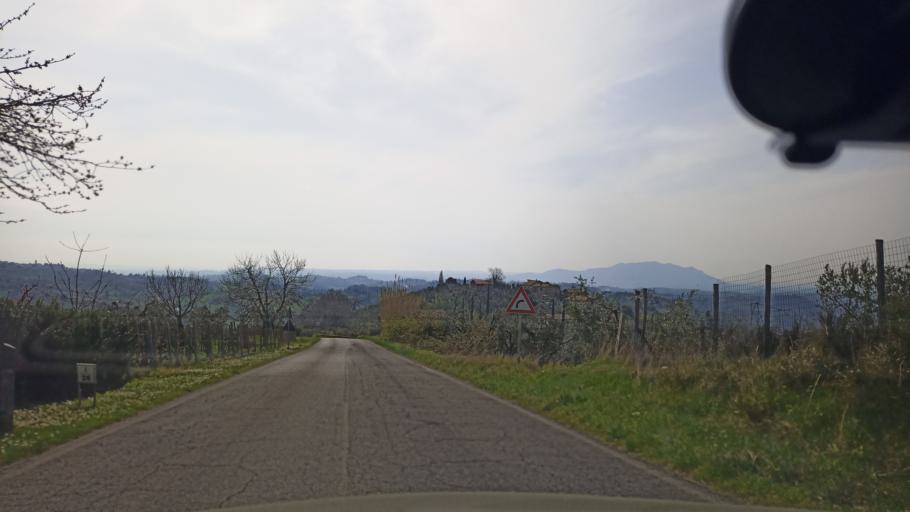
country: IT
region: Latium
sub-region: Provincia di Rieti
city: Torri in Sabina
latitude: 42.3377
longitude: 12.6500
